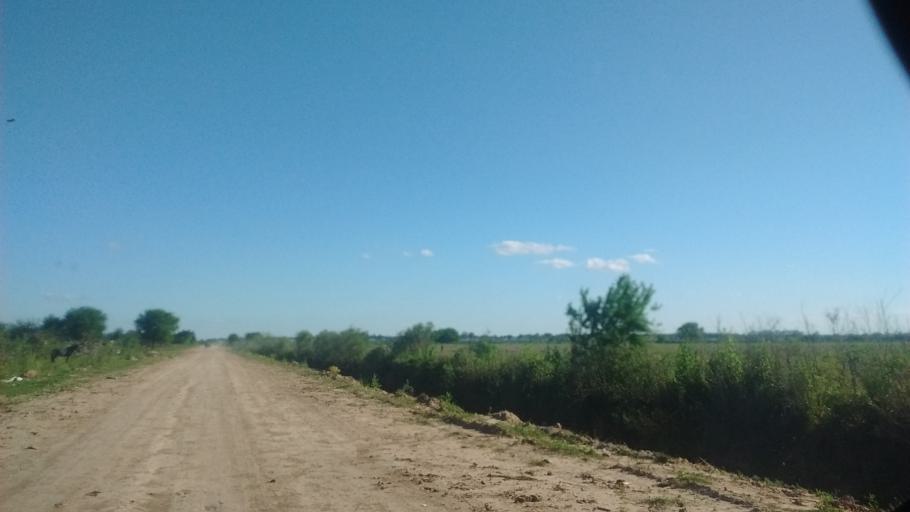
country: AR
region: Santa Fe
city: Funes
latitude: -32.8876
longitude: -60.7979
